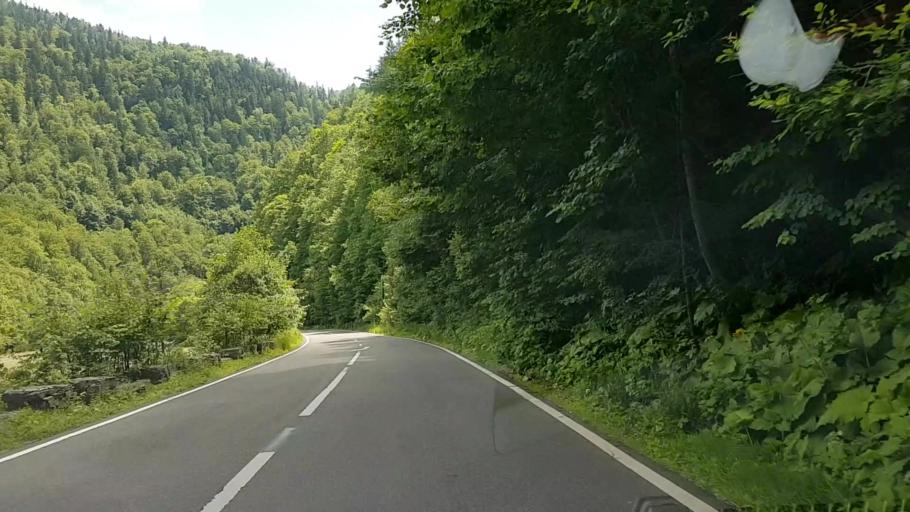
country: RO
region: Suceava
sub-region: Comuna Crucea
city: Crucea
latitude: 47.3136
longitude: 25.6264
